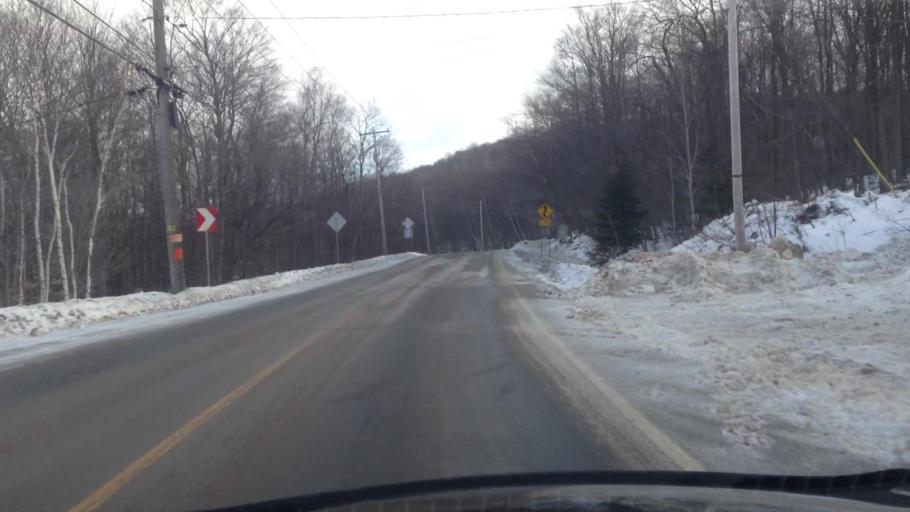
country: CA
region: Quebec
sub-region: Laurentides
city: Sainte-Agathe-des-Monts
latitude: 45.9223
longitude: -74.4992
